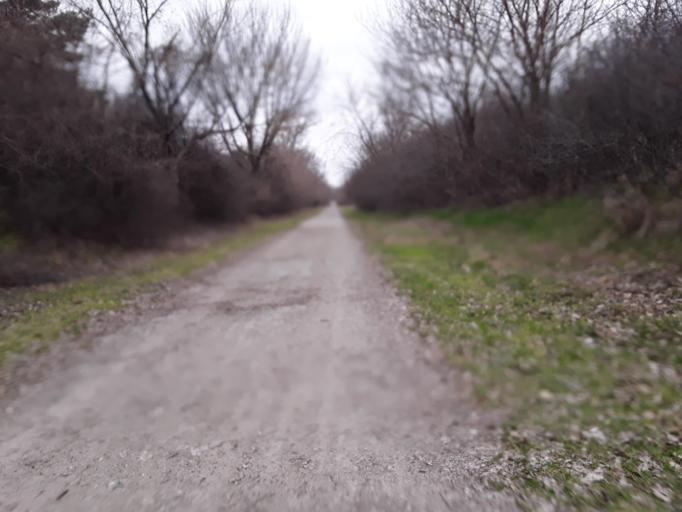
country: US
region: Nebraska
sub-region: Lancaster County
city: Lincoln
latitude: 40.8514
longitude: -96.6153
